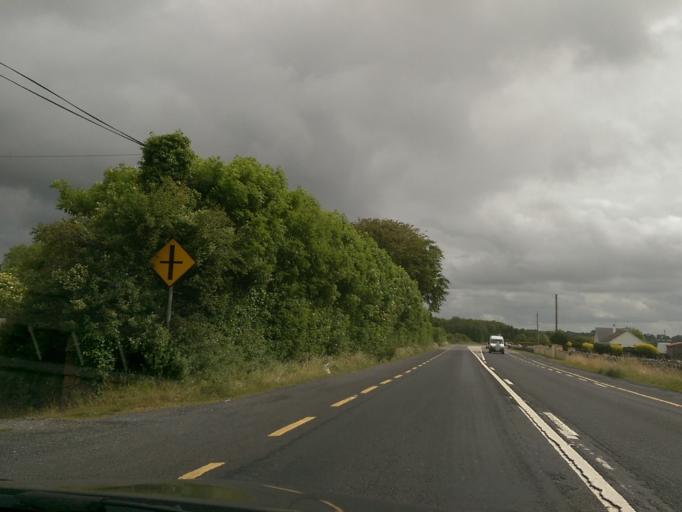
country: IE
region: Connaught
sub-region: County Galway
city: Loughrea
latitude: 53.2123
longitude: -8.5056
